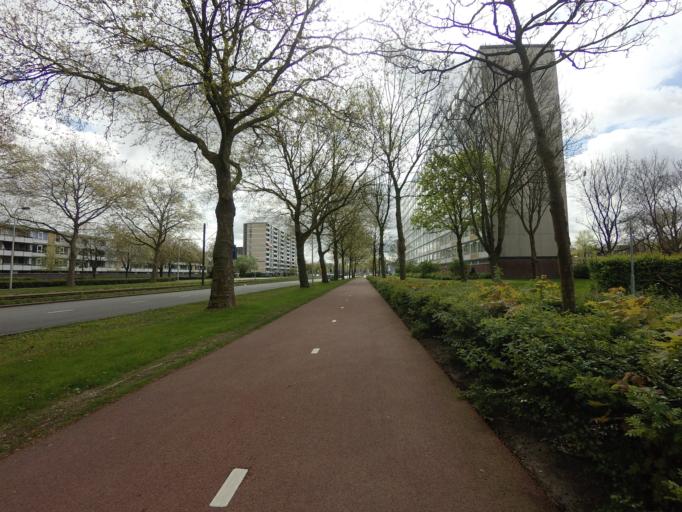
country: NL
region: Utrecht
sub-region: Gemeente Utrecht
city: Utrecht
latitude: 52.0770
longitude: 5.0942
